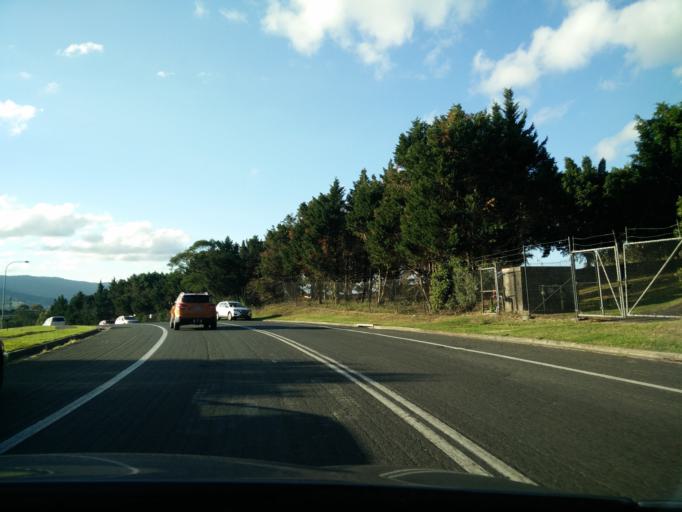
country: AU
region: New South Wales
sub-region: Wollongong
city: Berkeley
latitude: -34.4678
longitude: 150.8463
